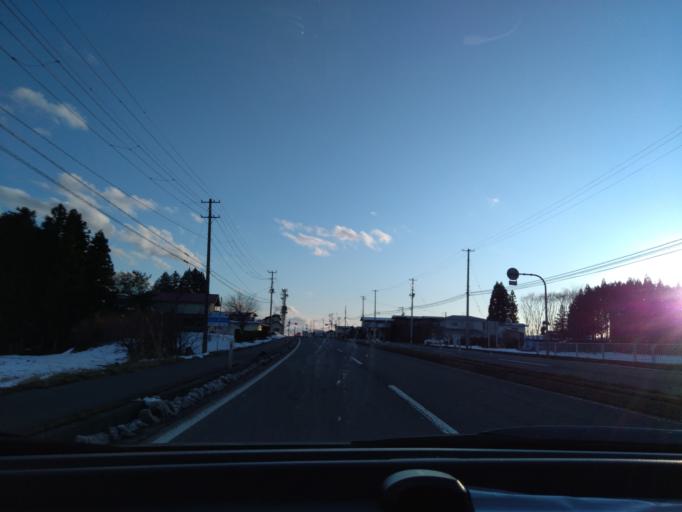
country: JP
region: Iwate
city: Hanamaki
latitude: 39.5288
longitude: 141.1636
